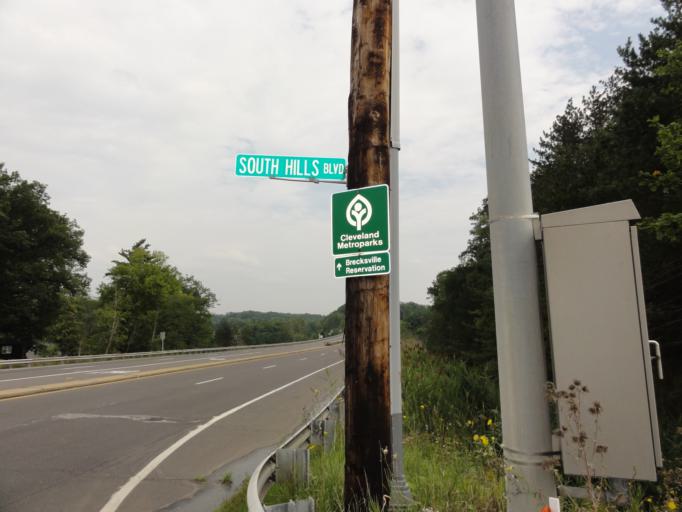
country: US
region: Ohio
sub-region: Cuyahoga County
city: Brecksville
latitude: 41.3187
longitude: -81.6429
